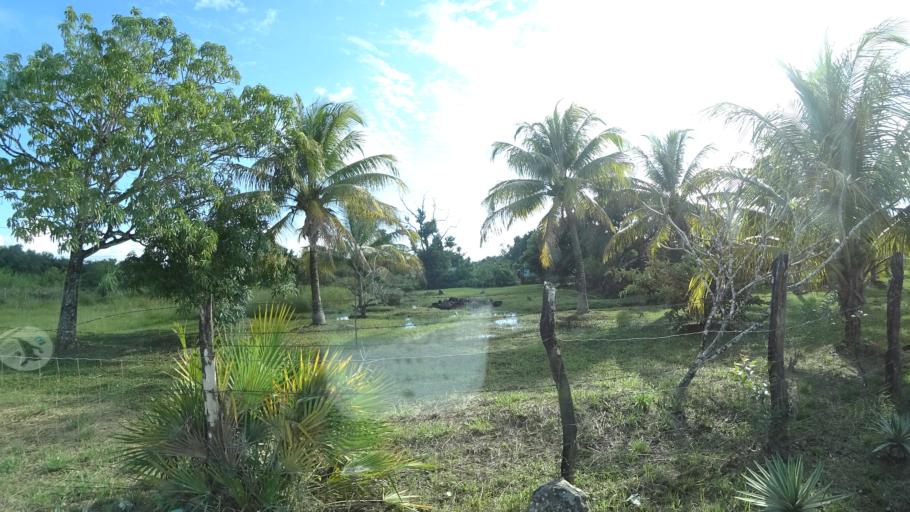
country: BZ
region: Belize
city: Belize City
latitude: 17.5566
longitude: -88.4059
